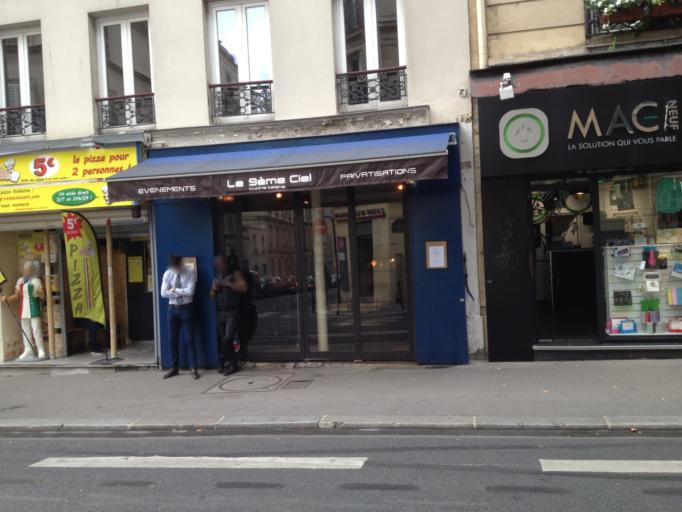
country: FR
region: Ile-de-France
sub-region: Paris
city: Saint-Ouen
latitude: 48.8810
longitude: 2.3464
